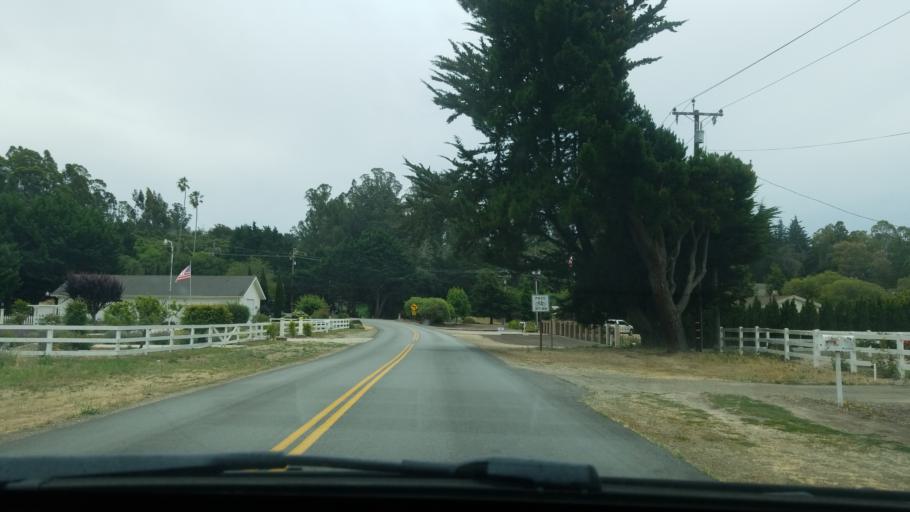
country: US
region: California
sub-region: San Luis Obispo County
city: Callender
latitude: 35.0770
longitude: -120.5430
